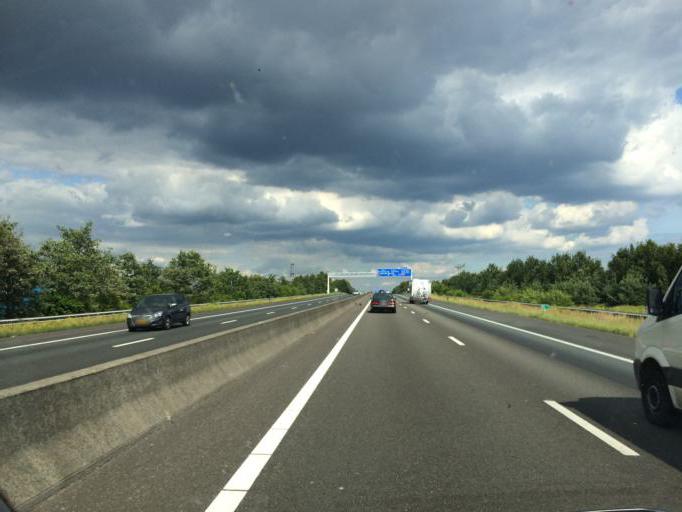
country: NL
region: Limburg
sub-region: Gemeente Venlo
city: Tegelen
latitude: 51.3937
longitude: 6.1046
